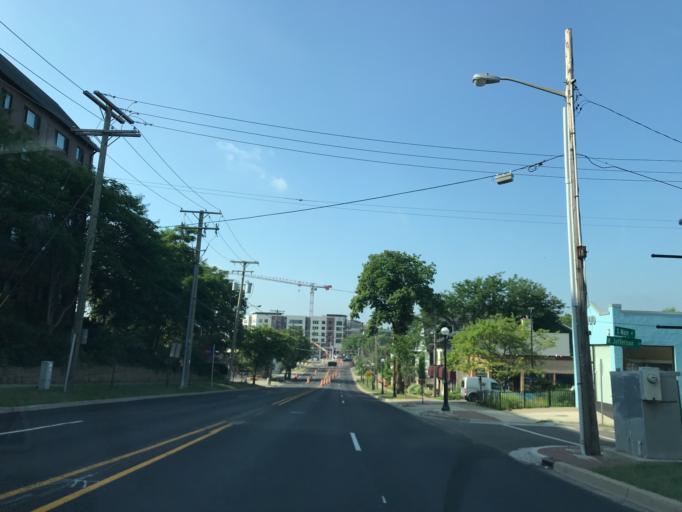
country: US
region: Michigan
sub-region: Washtenaw County
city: Ann Arbor
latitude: 42.2765
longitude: -83.7488
